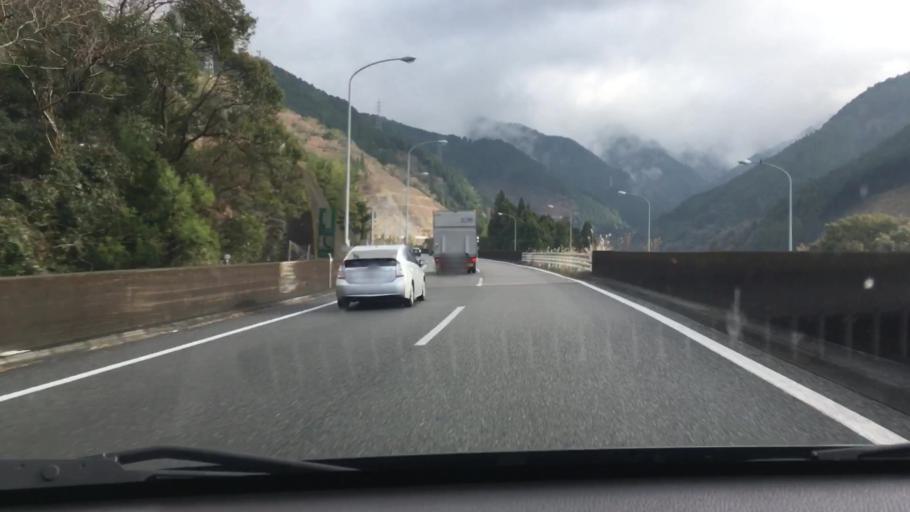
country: JP
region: Kumamoto
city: Yatsushiro
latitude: 32.4019
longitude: 130.6985
